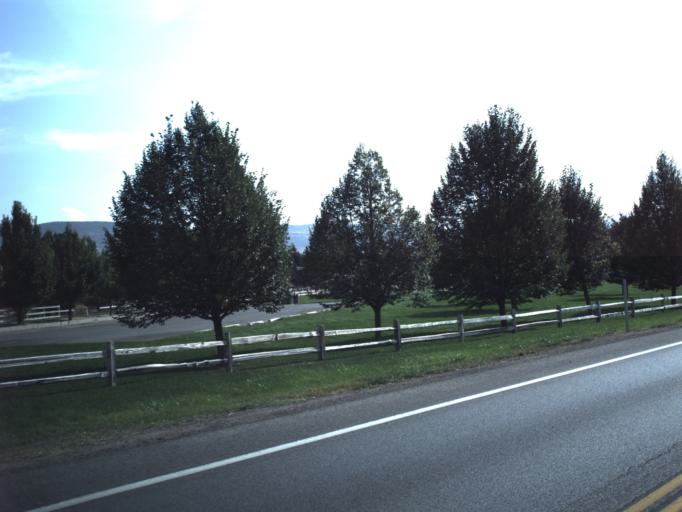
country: US
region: Utah
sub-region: Wasatch County
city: Midway
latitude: 40.5116
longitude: -111.4553
